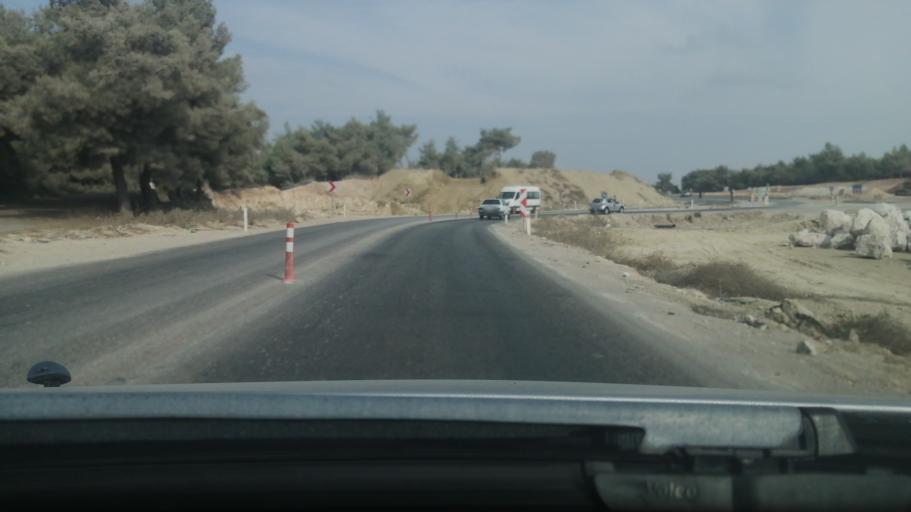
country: TR
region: Adana
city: Yuregir
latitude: 37.0817
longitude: 35.4768
